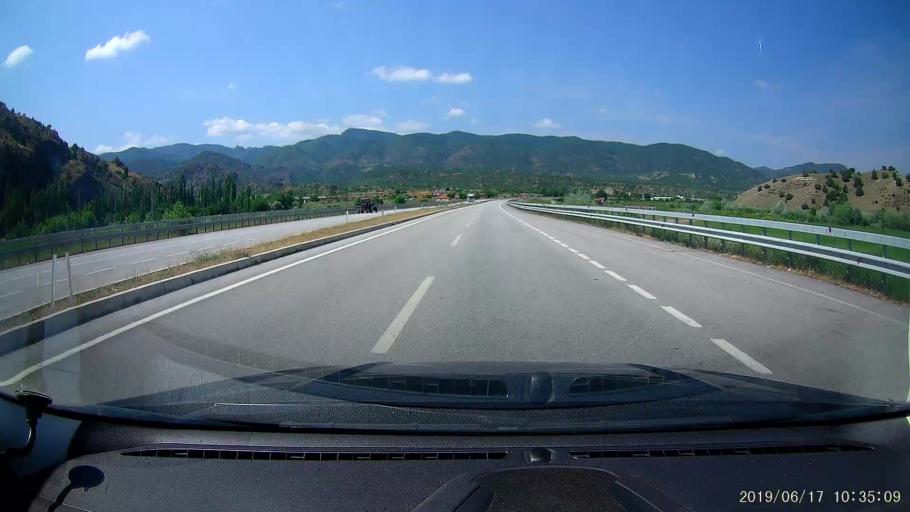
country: TR
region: Corum
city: Osmancik
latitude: 40.9764
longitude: 34.7096
